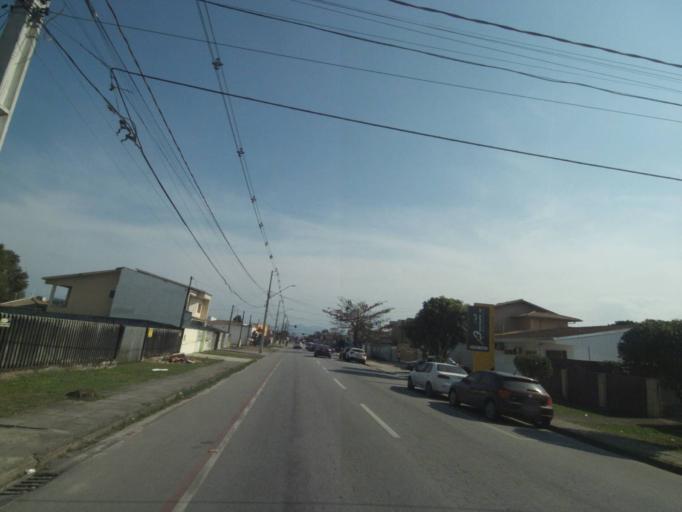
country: BR
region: Parana
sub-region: Paranagua
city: Paranagua
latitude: -25.5275
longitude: -48.5196
